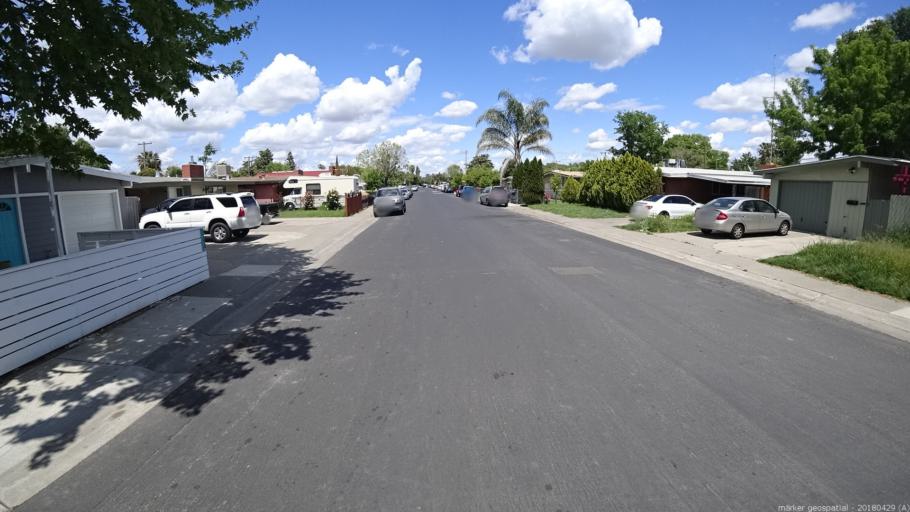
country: US
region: California
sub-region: Yolo County
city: West Sacramento
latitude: 38.5910
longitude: -121.5248
